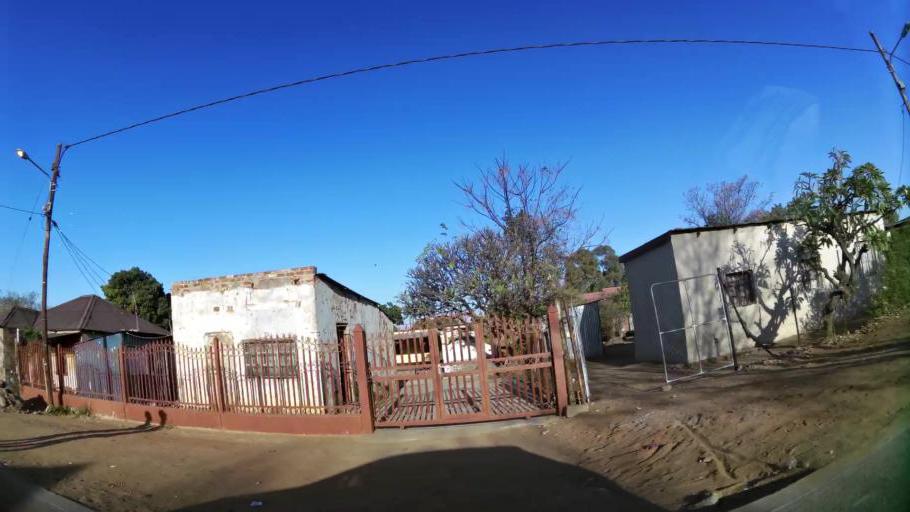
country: ZA
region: North-West
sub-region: Bojanala Platinum District Municipality
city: Rustenburg
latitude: -25.6458
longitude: 27.2179
